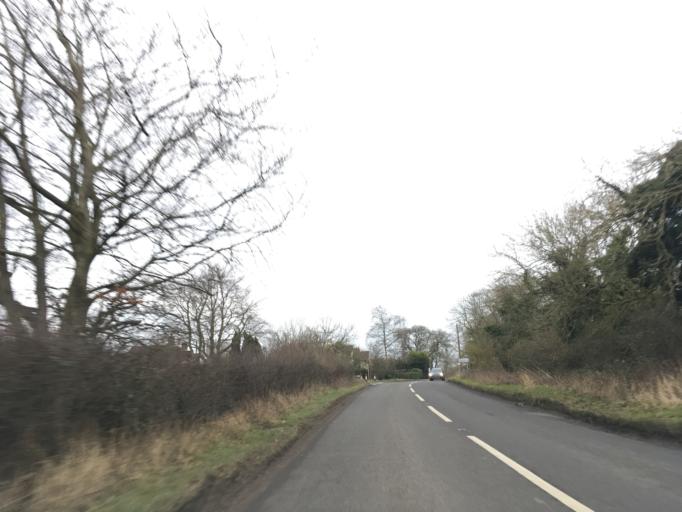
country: GB
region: England
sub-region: South Gloucestershire
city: Yate
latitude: 51.5127
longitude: -2.4121
